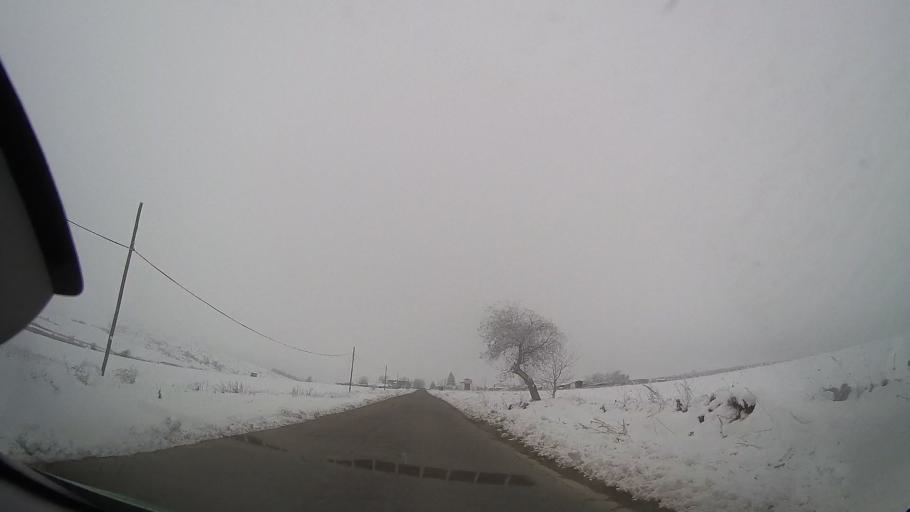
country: RO
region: Neamt
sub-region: Comuna Icusesti
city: Balusesti
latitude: 46.8557
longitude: 27.0319
